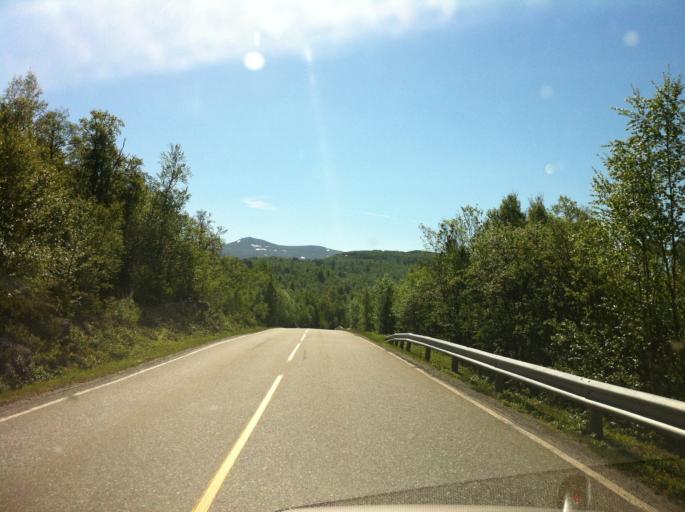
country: NO
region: Sor-Trondelag
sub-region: Roros
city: Roros
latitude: 62.6185
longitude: 11.8403
